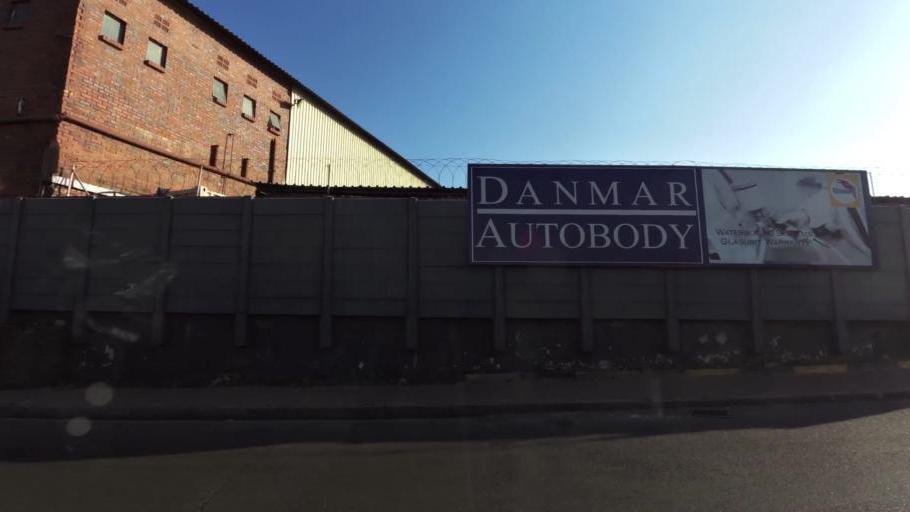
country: ZA
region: Gauteng
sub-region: City of Johannesburg Metropolitan Municipality
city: Johannesburg
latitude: -26.2268
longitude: 28.0281
